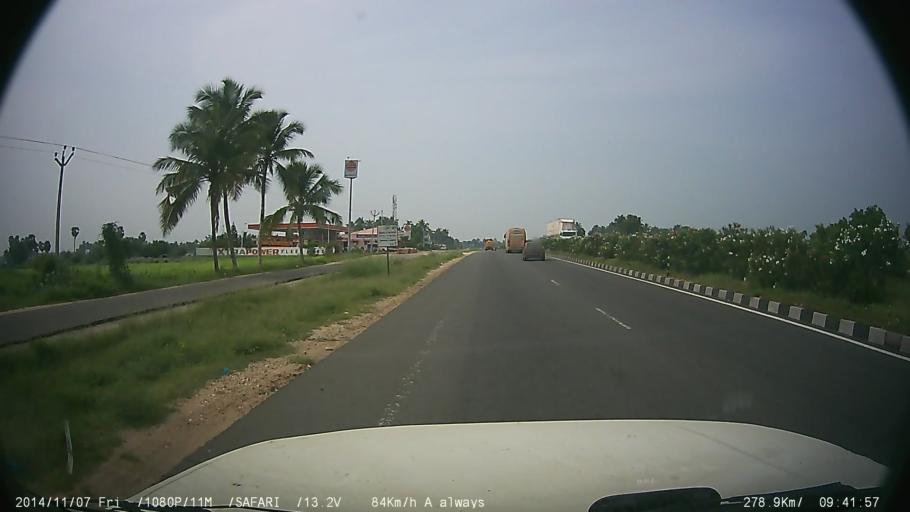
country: IN
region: Tamil Nadu
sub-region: Erode
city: Perundurai
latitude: 11.3138
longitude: 77.6127
